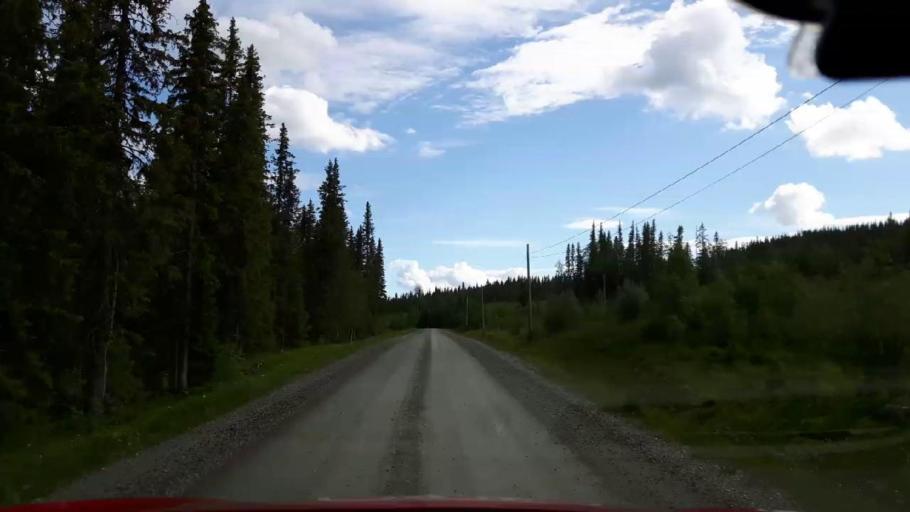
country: SE
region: Jaemtland
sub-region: Krokoms Kommun
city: Valla
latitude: 63.8228
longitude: 14.0409
